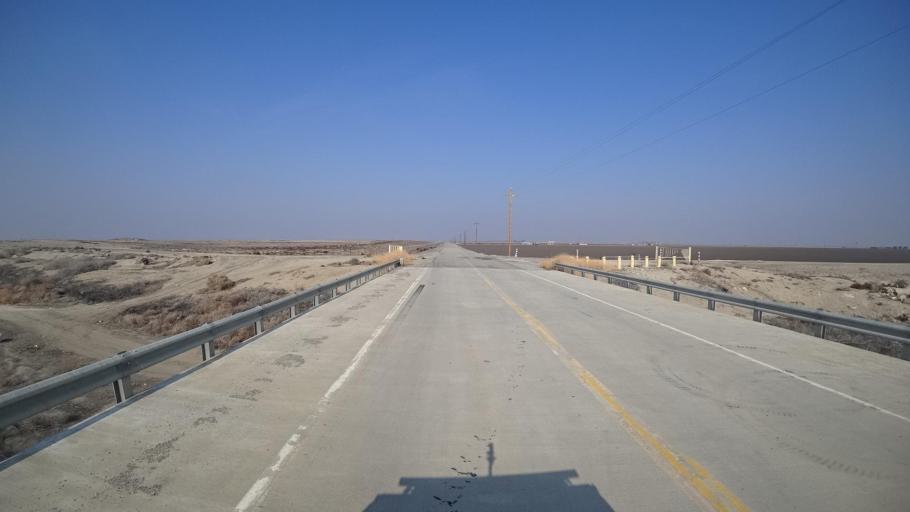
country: US
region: California
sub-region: Kern County
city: Buttonwillow
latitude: 35.3138
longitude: -119.3767
